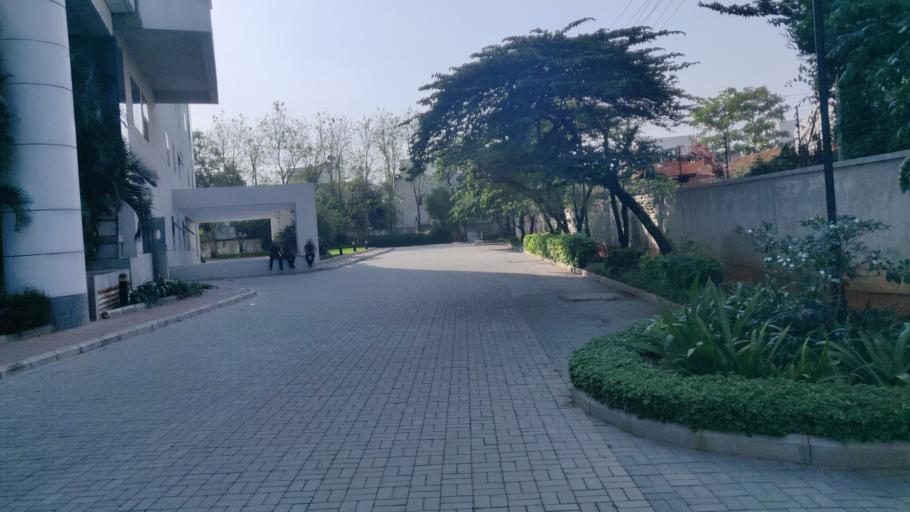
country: IN
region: Telangana
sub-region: Medak
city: Serilingampalle
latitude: 17.4279
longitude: 78.3318
